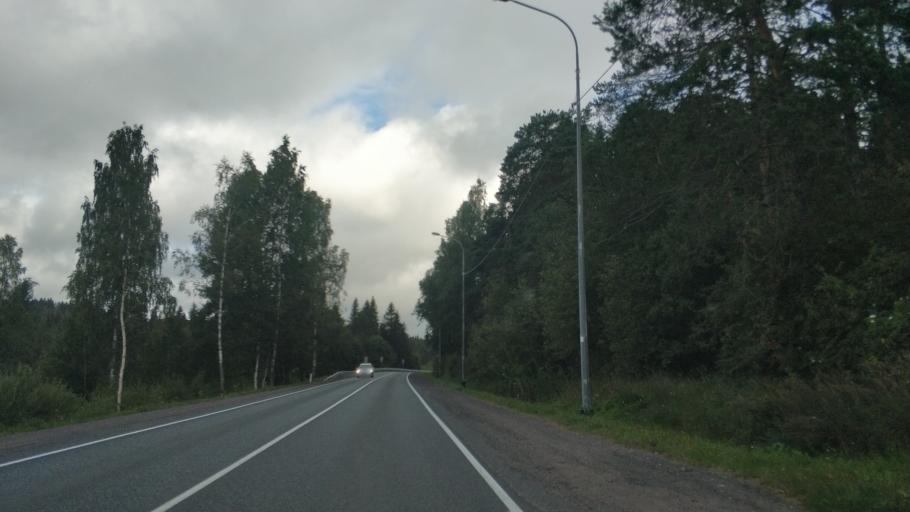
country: RU
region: Republic of Karelia
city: Khelyulya
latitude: 61.7539
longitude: 30.6581
